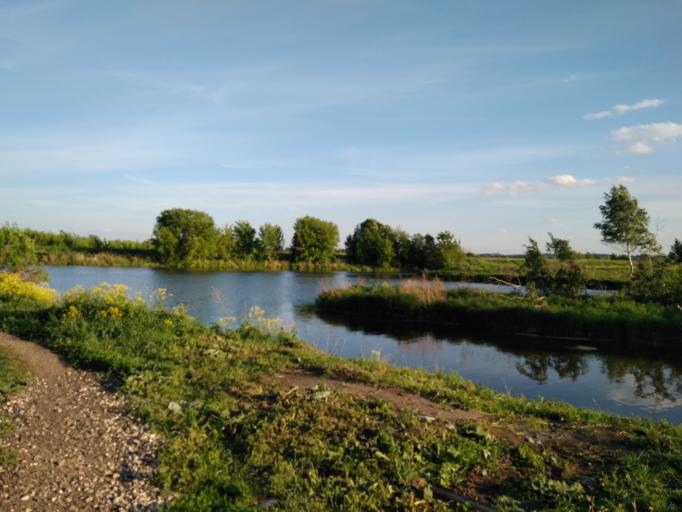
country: RU
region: Moskovskaya
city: Zhukovskiy
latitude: 55.5828
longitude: 38.0996
